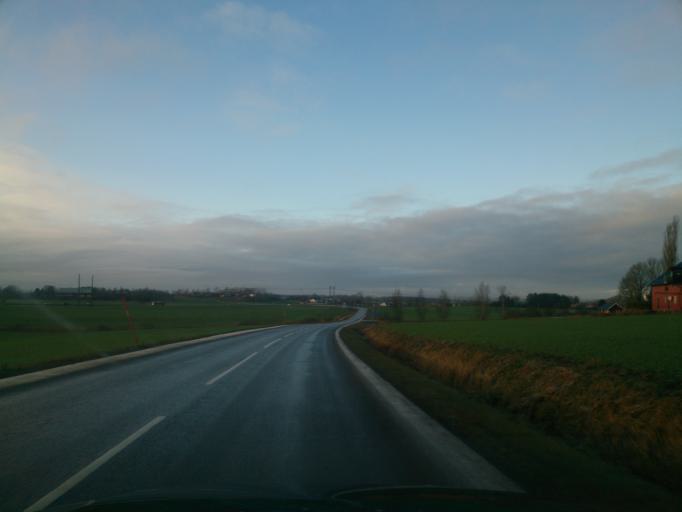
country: SE
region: OEstergoetland
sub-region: Linkopings Kommun
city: Linghem
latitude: 58.3984
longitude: 15.7787
